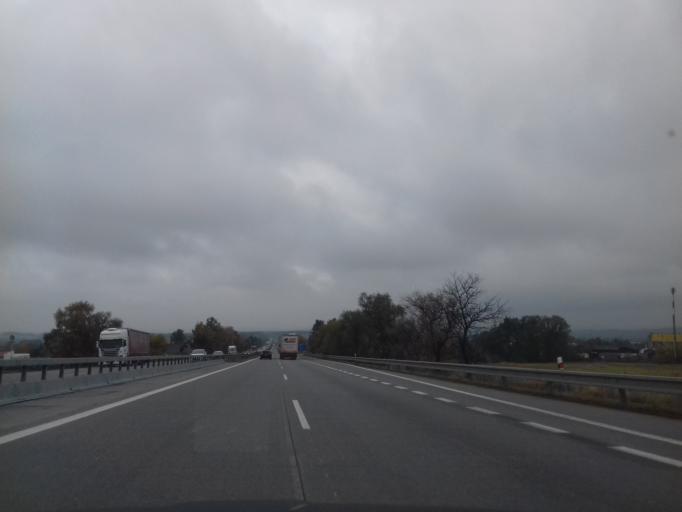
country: CZ
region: Central Bohemia
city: Cechtice
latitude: 49.6543
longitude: 15.1227
